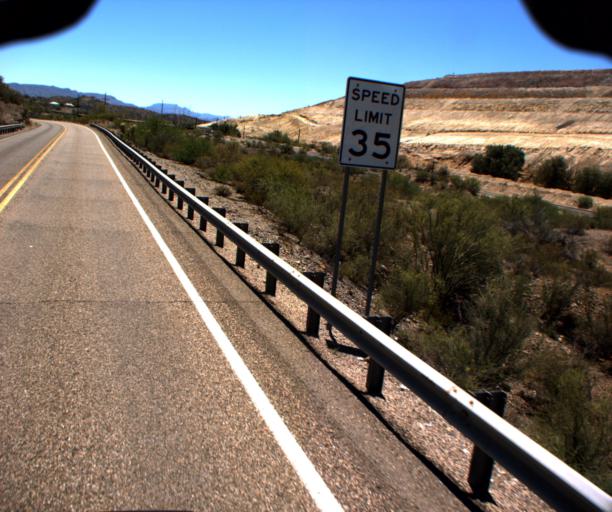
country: US
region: Arizona
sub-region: Pinal County
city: Kearny
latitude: 33.0043
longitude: -110.7959
